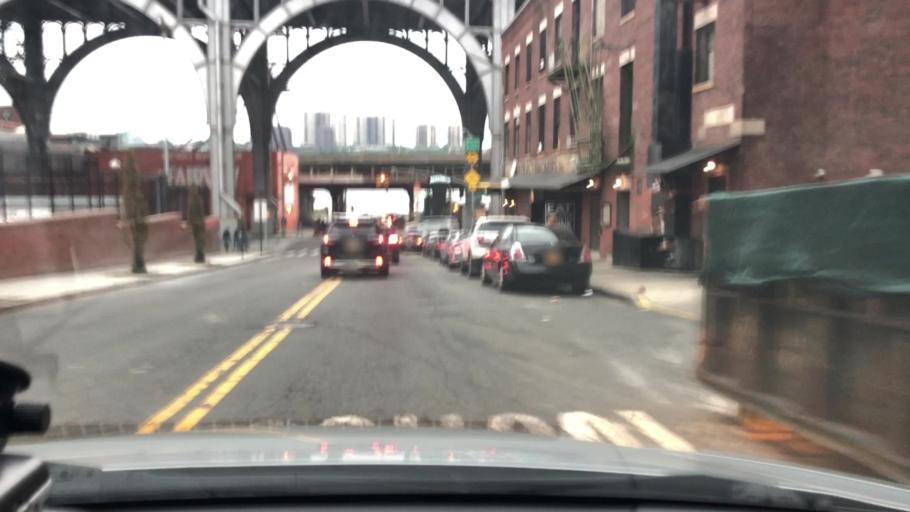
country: US
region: New Jersey
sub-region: Bergen County
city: Edgewater
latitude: 40.8197
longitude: -73.9581
